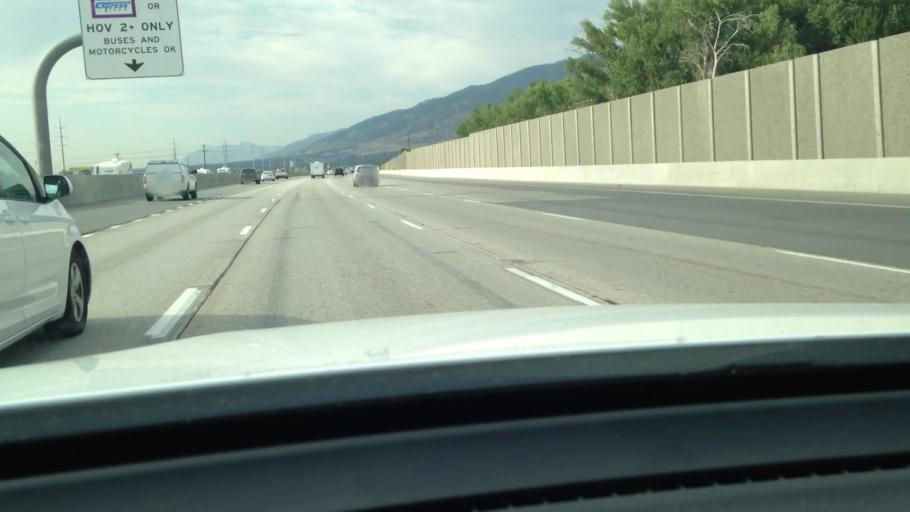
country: US
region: Utah
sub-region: Davis County
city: Centerville
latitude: 40.9259
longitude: -111.8911
